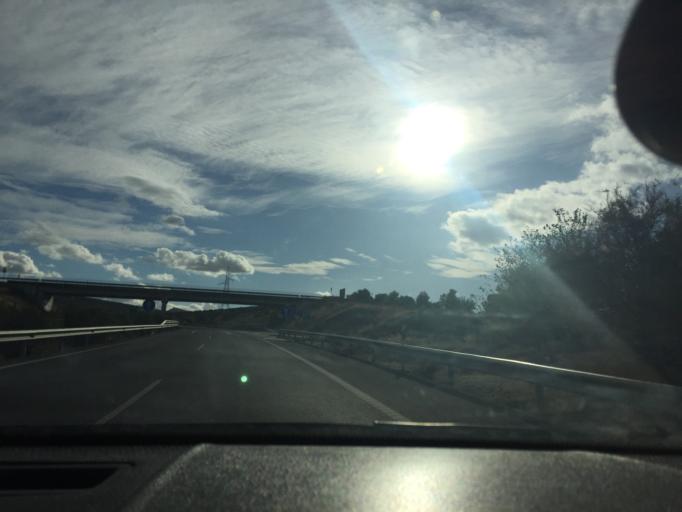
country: ES
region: Andalusia
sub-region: Provincia de Jaen
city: Torre del Campo
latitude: 37.7780
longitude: -3.9024
